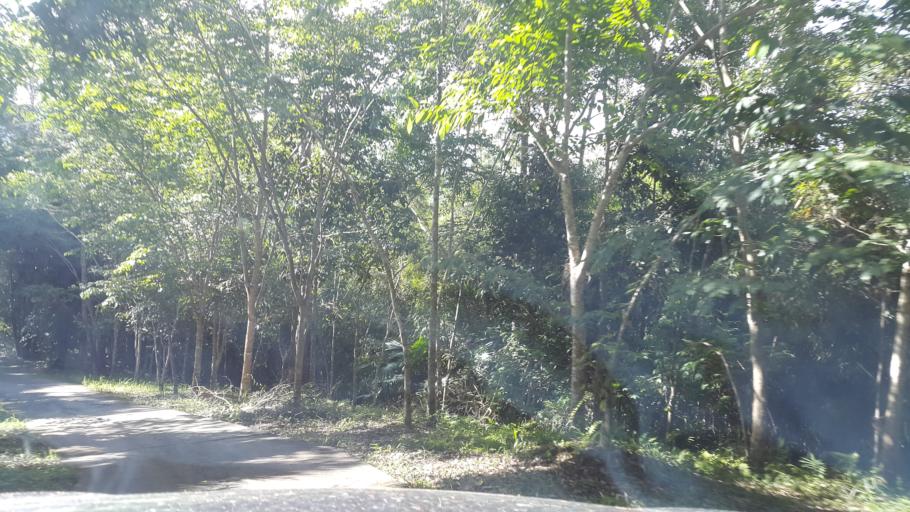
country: TH
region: Loei
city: Na Haeo
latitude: 17.5580
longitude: 100.9542
